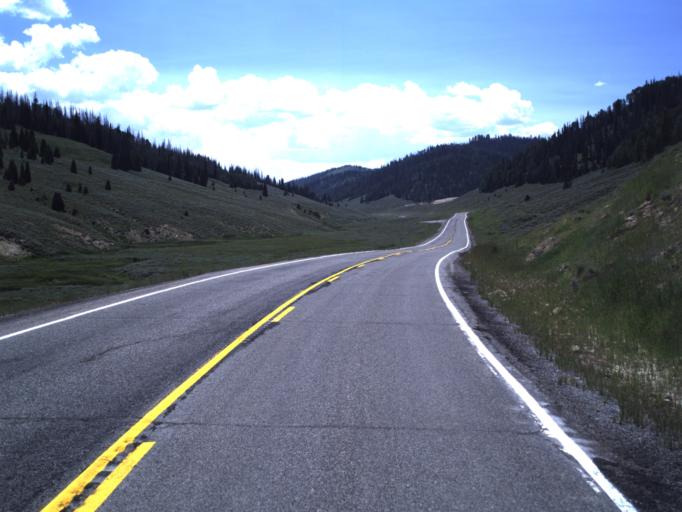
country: US
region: Utah
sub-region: Sanpete County
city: Fairview
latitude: 39.6804
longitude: -111.2431
